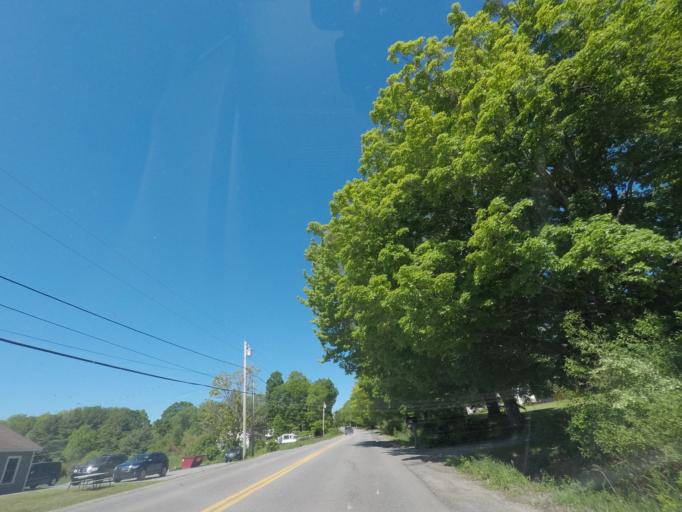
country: US
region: Maine
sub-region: Kennebec County
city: Gardiner
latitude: 44.2314
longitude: -69.7932
